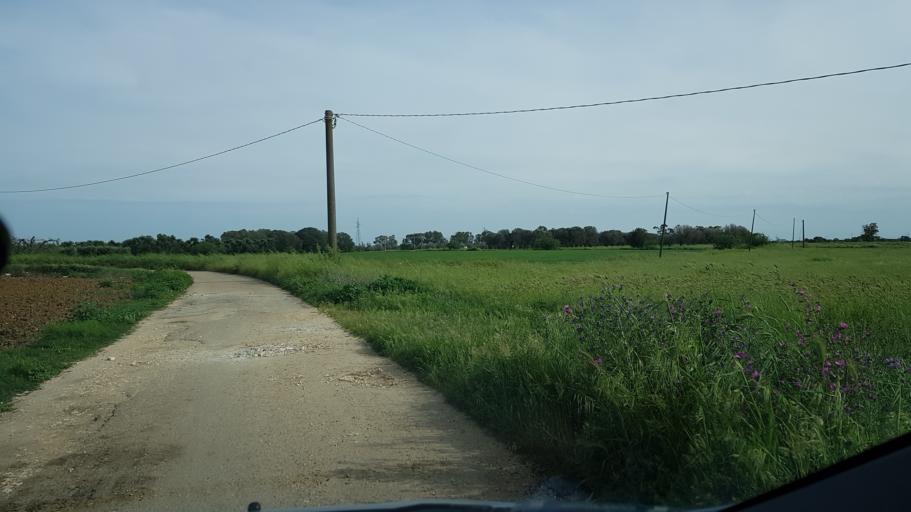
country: IT
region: Apulia
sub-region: Provincia di Brindisi
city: Tuturano
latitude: 40.5518
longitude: 17.9316
